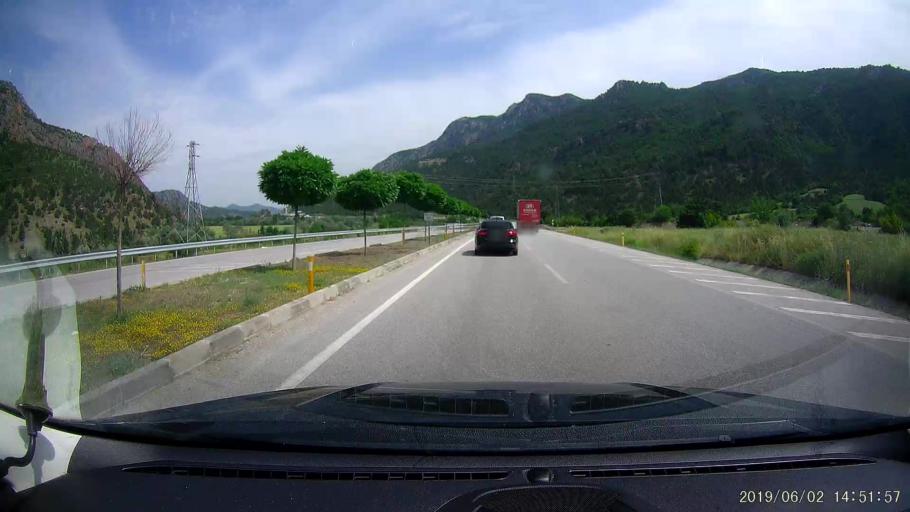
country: TR
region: Corum
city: Hacihamza
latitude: 41.0526
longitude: 34.5466
